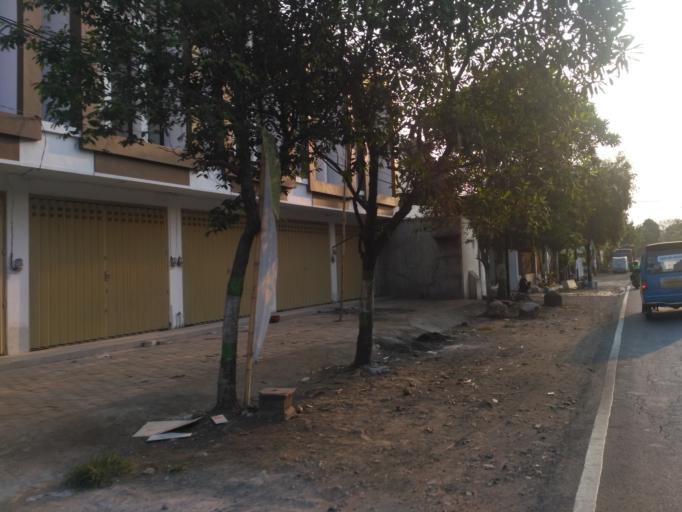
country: ID
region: East Java
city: Kepuh
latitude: -8.0014
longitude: 112.6210
